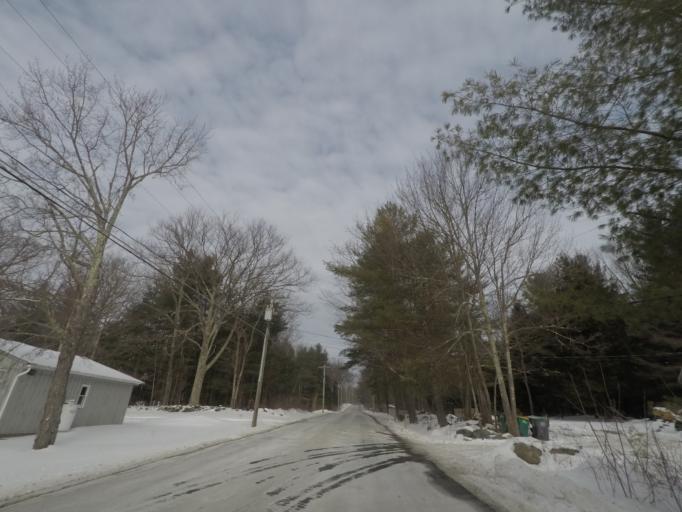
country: US
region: New York
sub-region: Rensselaer County
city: Averill Park
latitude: 42.5892
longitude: -73.4863
